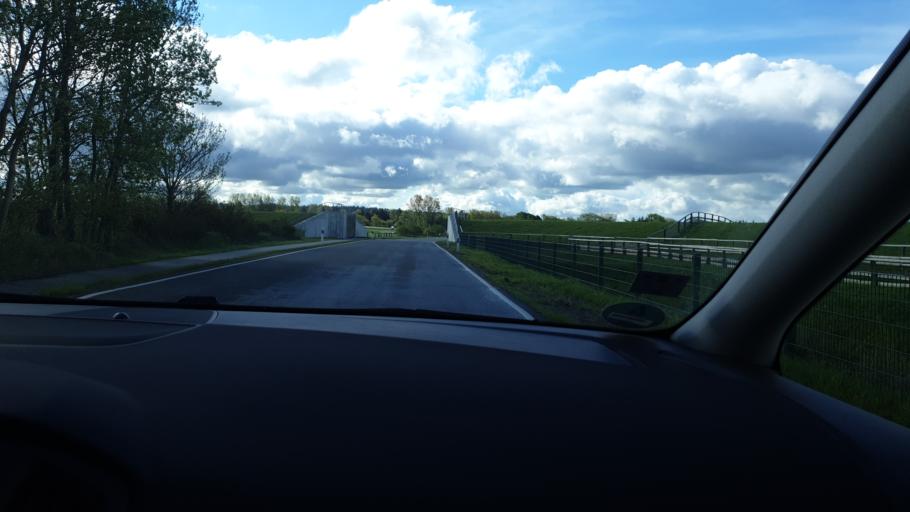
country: DE
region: Schleswig-Holstein
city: Wobbenbull
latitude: 54.5225
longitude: 8.9945
